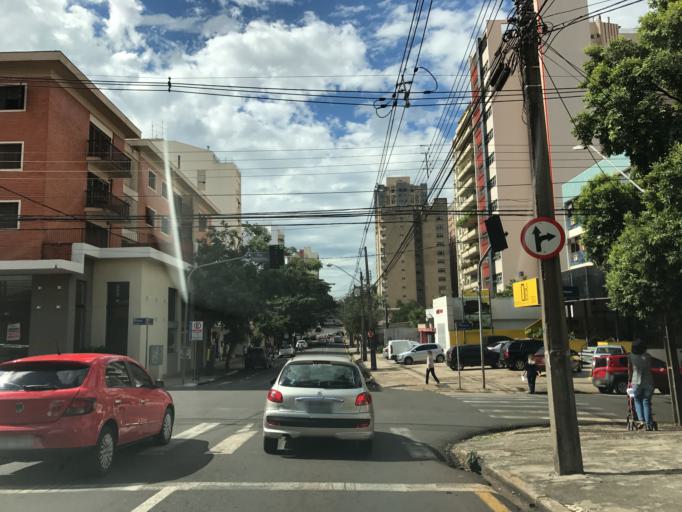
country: BR
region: Parana
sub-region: Londrina
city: Londrina
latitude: -23.3154
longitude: -51.1630
